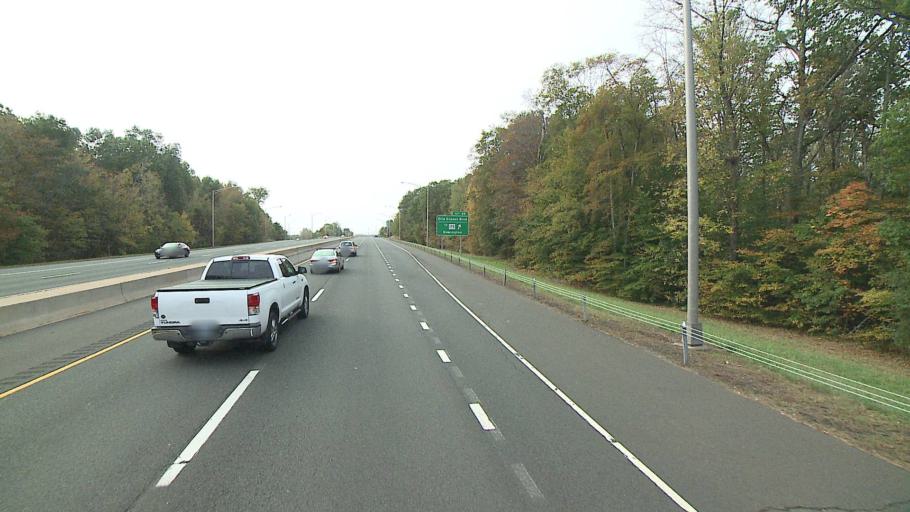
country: US
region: Connecticut
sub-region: Hartford County
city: Newington
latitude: 41.7041
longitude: -72.7579
